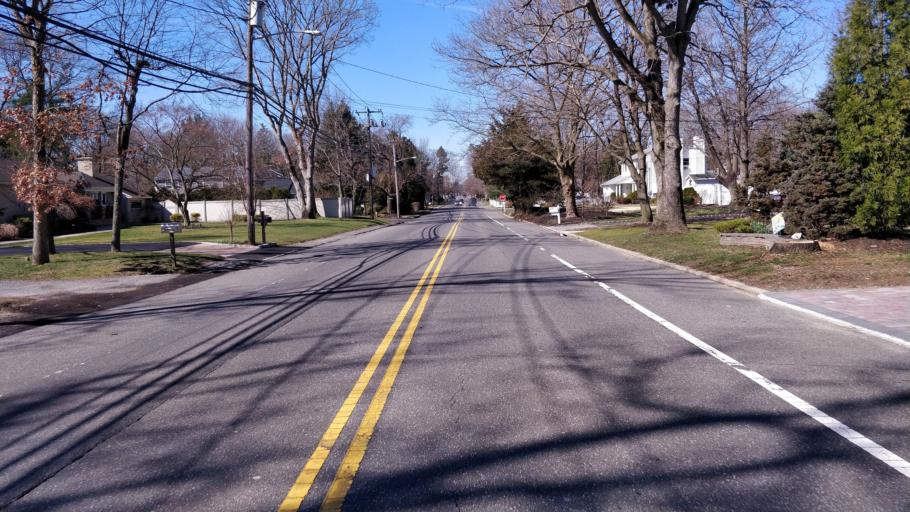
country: US
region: New York
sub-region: Suffolk County
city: Commack
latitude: 40.8513
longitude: -73.2992
